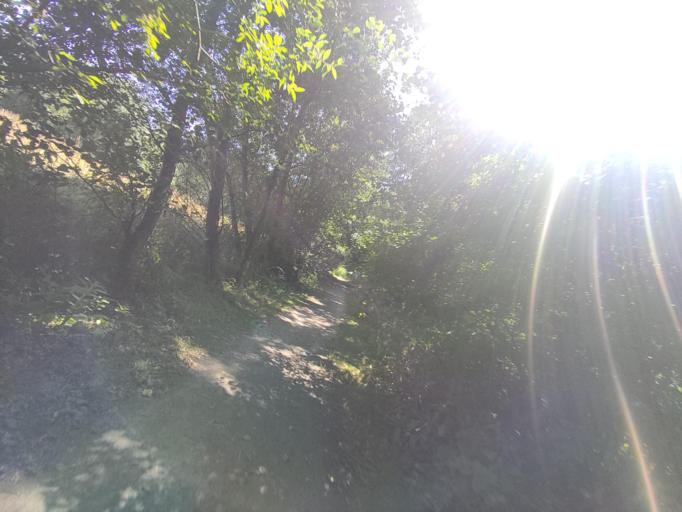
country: FR
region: Nord-Pas-de-Calais
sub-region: Departement du Pas-de-Calais
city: Maroeuil
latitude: 50.3171
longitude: 2.7059
